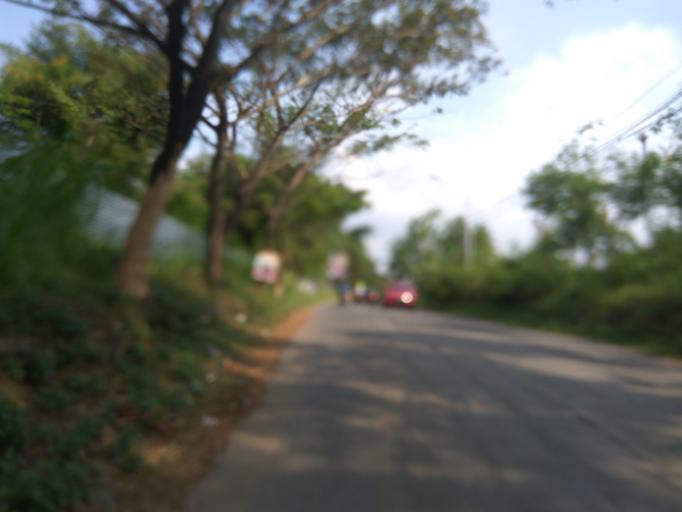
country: ID
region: Central Java
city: Semarang
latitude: -7.0347
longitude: 110.3912
